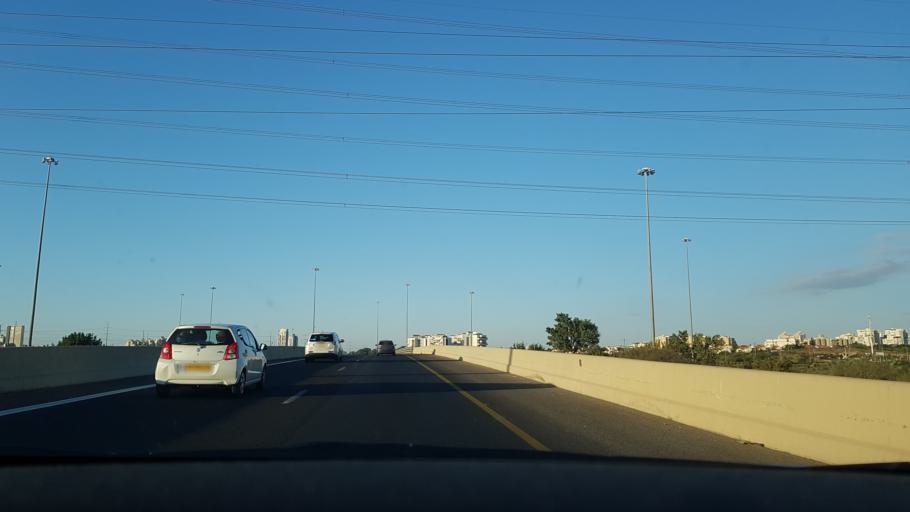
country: IL
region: Central District
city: Rishon LeZiyyon
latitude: 31.9514
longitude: 34.7846
